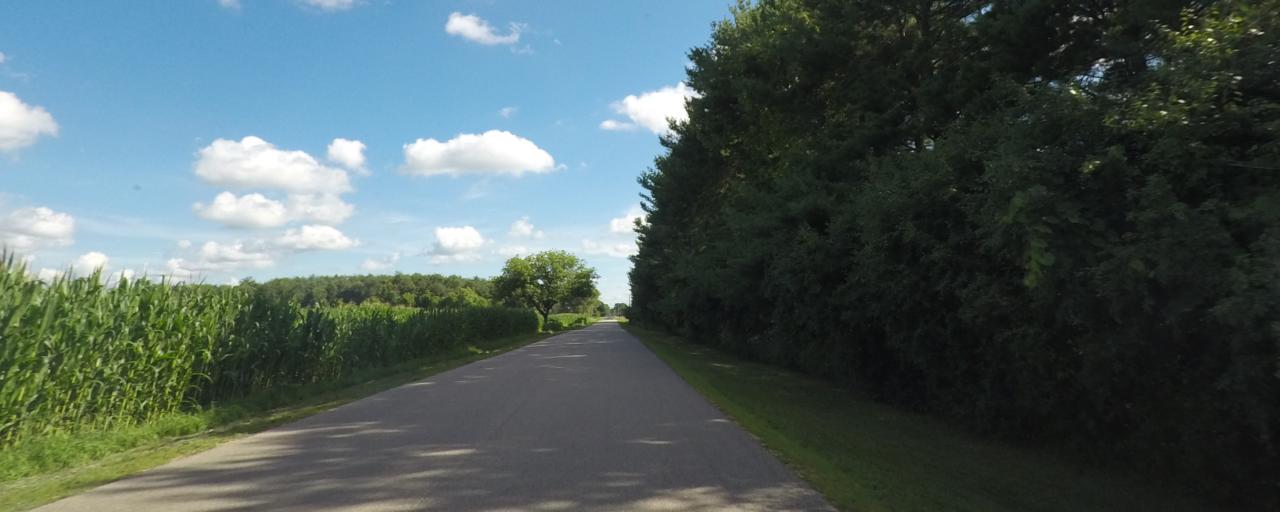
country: US
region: Wisconsin
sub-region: Rock County
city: Edgerton
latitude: 42.8937
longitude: -89.1320
